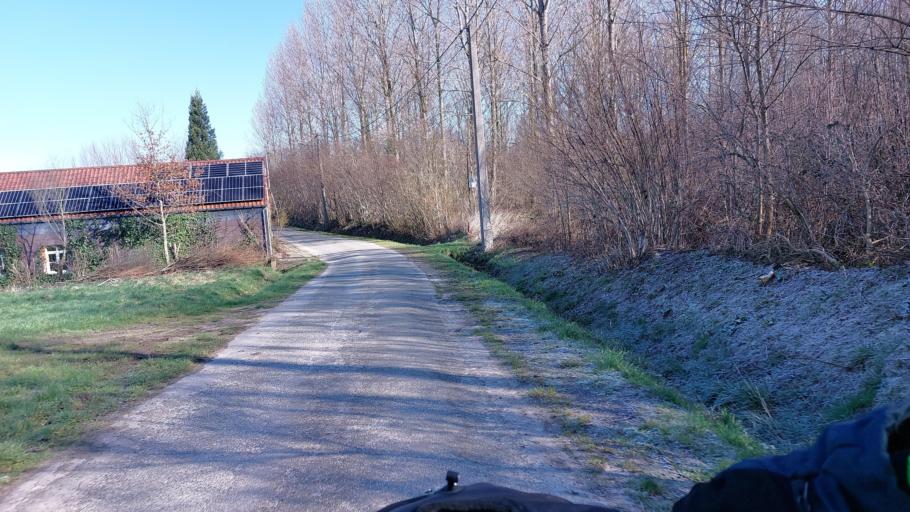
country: BE
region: Wallonia
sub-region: Province du Hainaut
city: Brugelette
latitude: 50.6227
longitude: 3.8712
